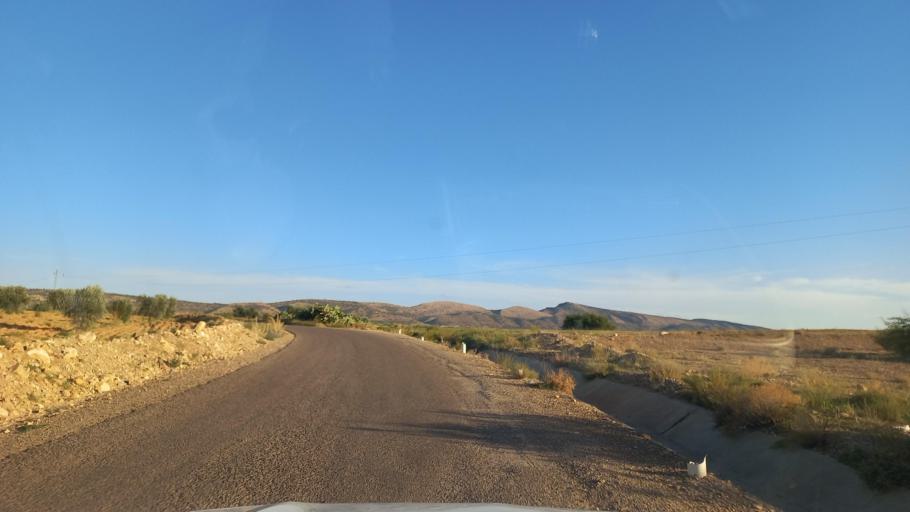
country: TN
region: Al Qasrayn
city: Sbiba
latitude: 35.4105
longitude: 9.1457
